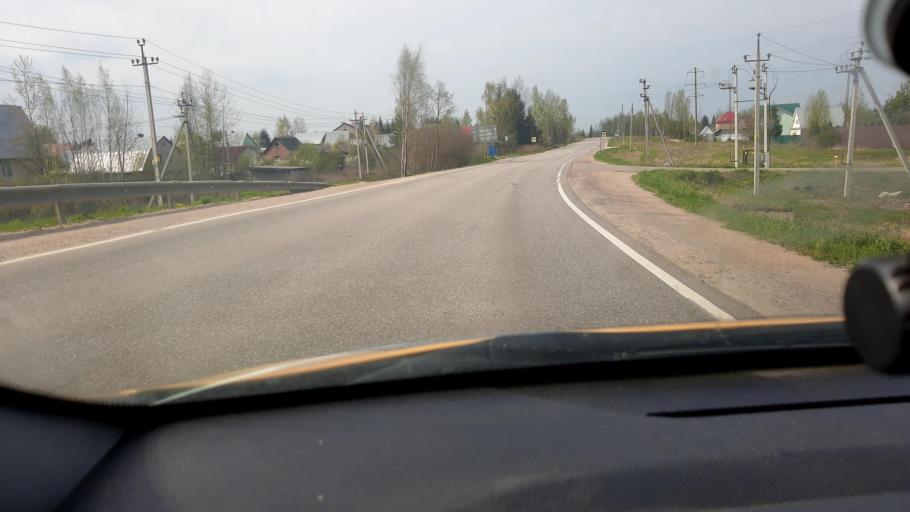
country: RU
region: Moskovskaya
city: Rumyantsevo
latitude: 55.9131
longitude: 36.5962
